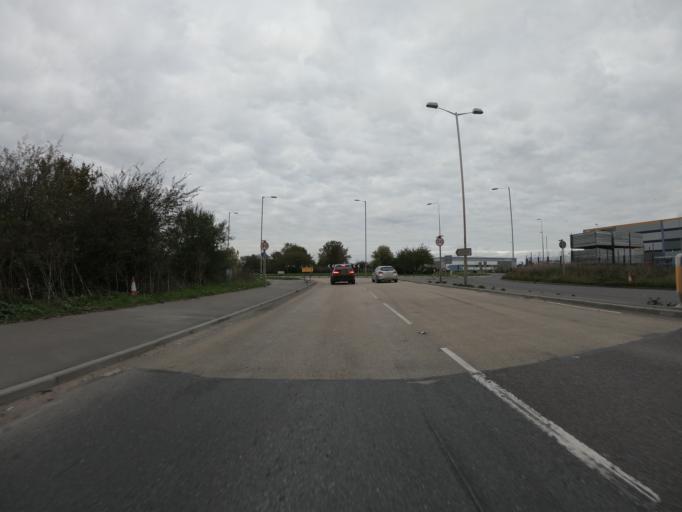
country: GB
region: England
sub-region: Borough of Thurrock
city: Tilbury
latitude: 51.4678
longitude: 0.3480
